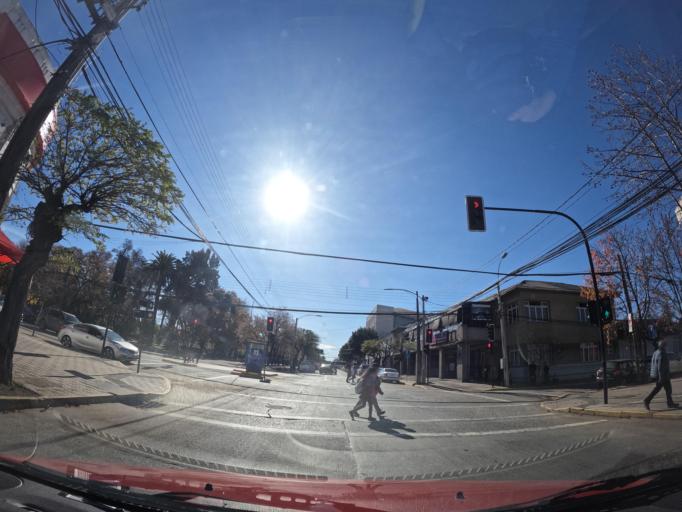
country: CL
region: Maule
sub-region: Provincia de Cauquenes
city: Cauquenes
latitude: -35.9678
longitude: -72.3147
